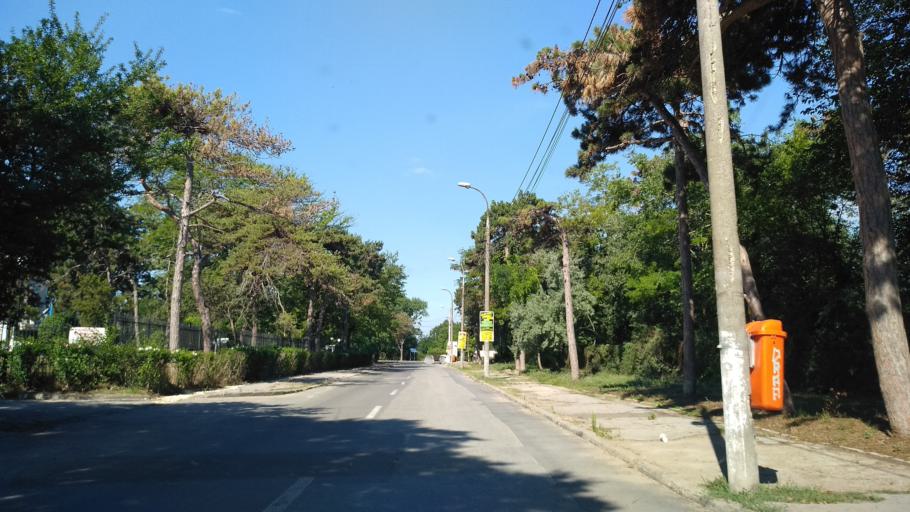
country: RO
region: Constanta
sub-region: Oras Eforie
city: Eforie
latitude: 44.0383
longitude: 28.6473
